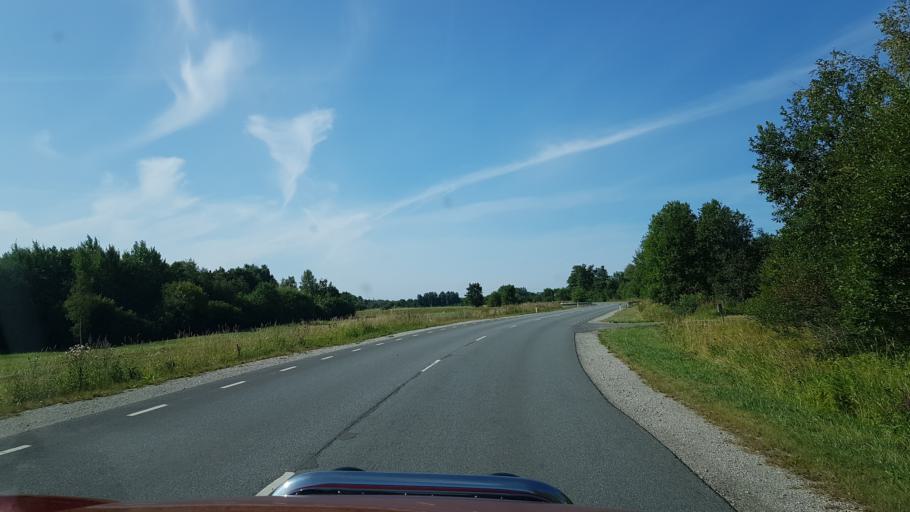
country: EE
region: Harju
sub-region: Rae vald
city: Jueri
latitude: 59.3779
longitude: 24.9280
